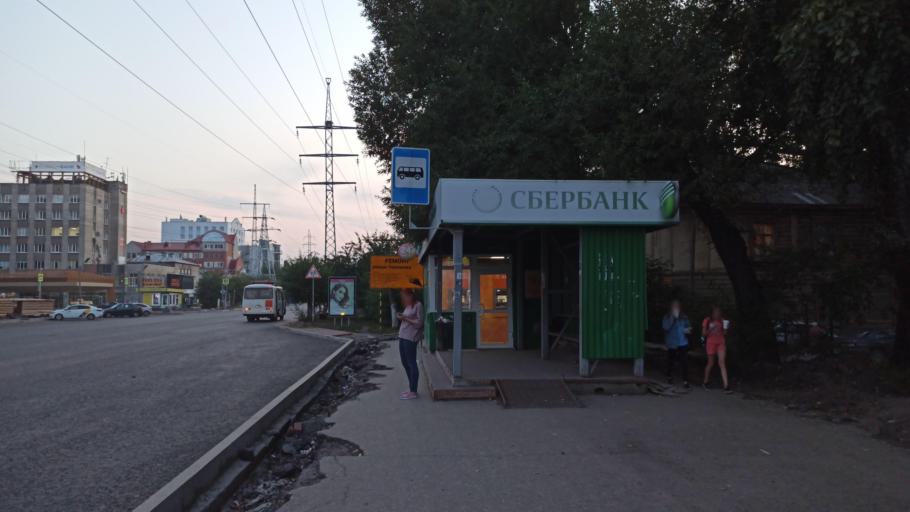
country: RU
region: Tomsk
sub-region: Tomskiy Rayon
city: Tomsk
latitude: 56.4552
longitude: 84.9733
